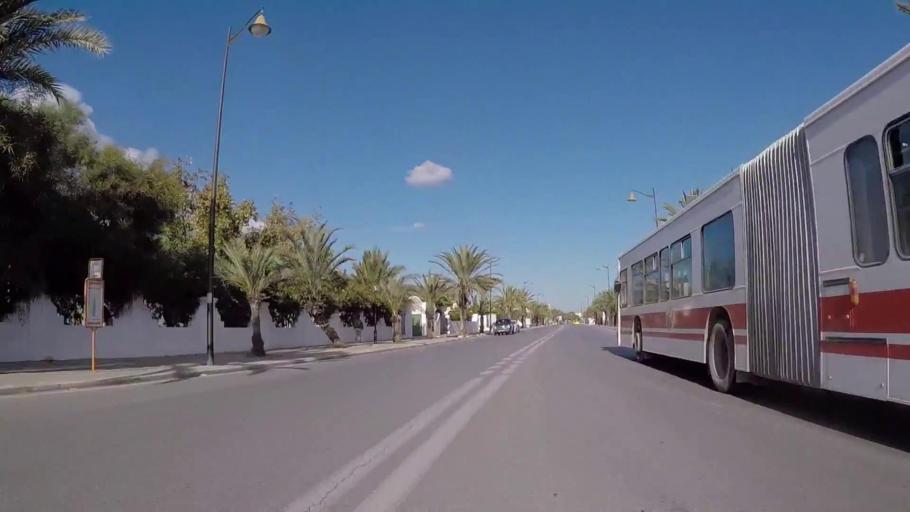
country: TN
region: Nabul
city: Al Hammamat
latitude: 36.3626
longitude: 10.5318
